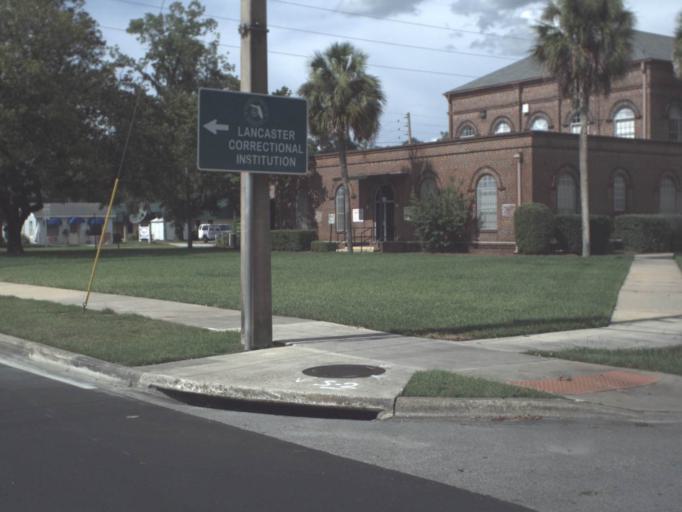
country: US
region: Florida
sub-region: Gilchrist County
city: Trenton
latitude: 29.6127
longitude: -82.8183
